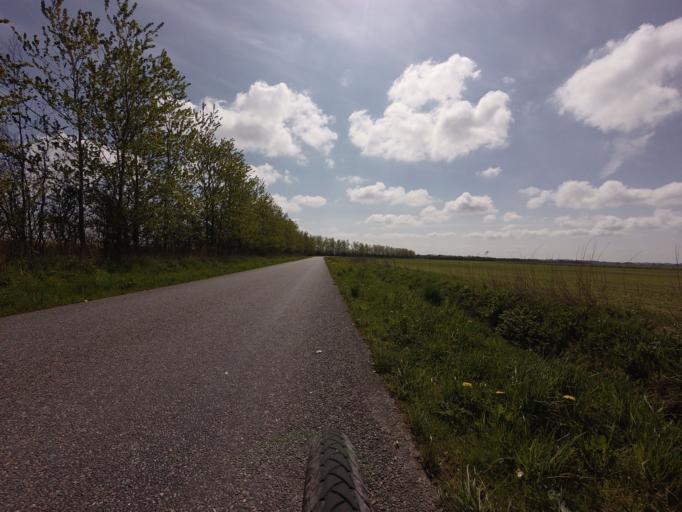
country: DK
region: North Denmark
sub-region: Jammerbugt Kommune
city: Brovst
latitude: 57.1396
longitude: 9.5235
